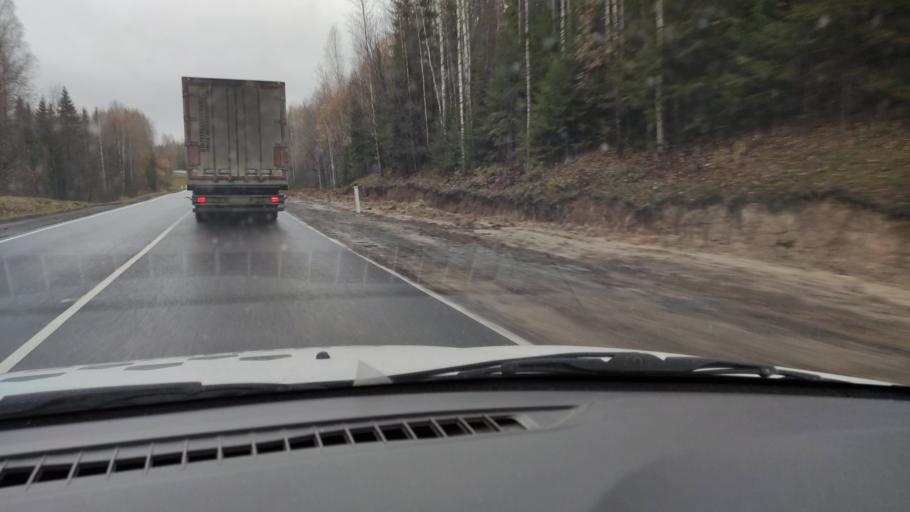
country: RU
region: Kirov
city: Omutninsk
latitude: 58.7459
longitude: 52.0626
